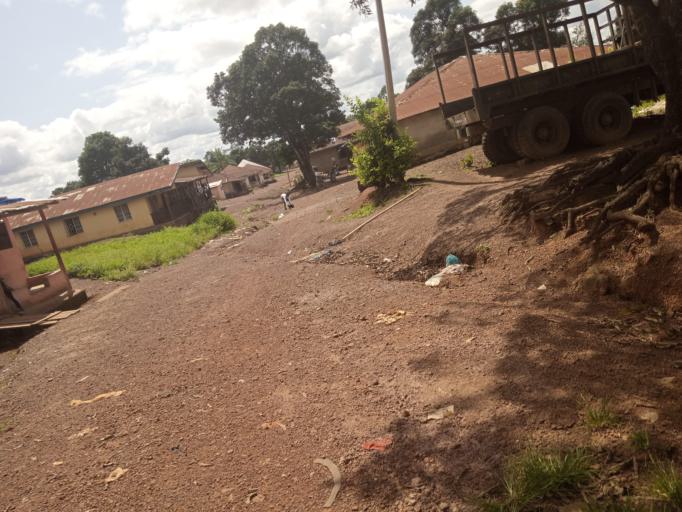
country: SL
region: Northern Province
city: Kamakwie
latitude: 9.4962
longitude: -12.2411
